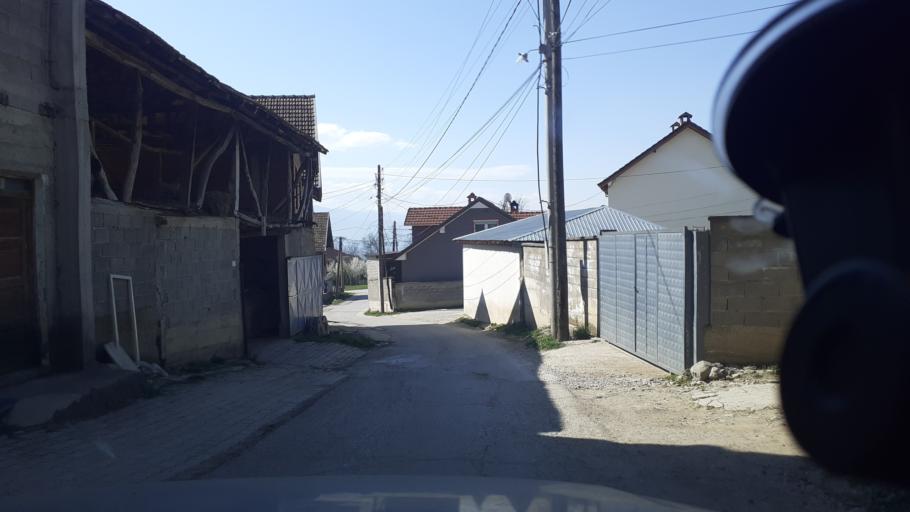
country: MK
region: Tearce
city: Slatino
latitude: 42.0649
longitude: 21.0351
